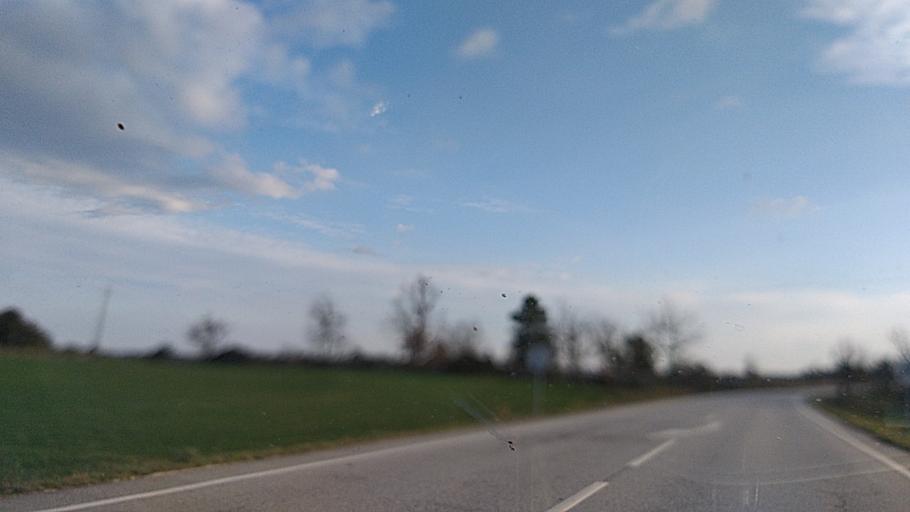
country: ES
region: Castille and Leon
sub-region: Provincia de Salamanca
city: Fuentes de Onoro
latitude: 40.6309
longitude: -6.9731
